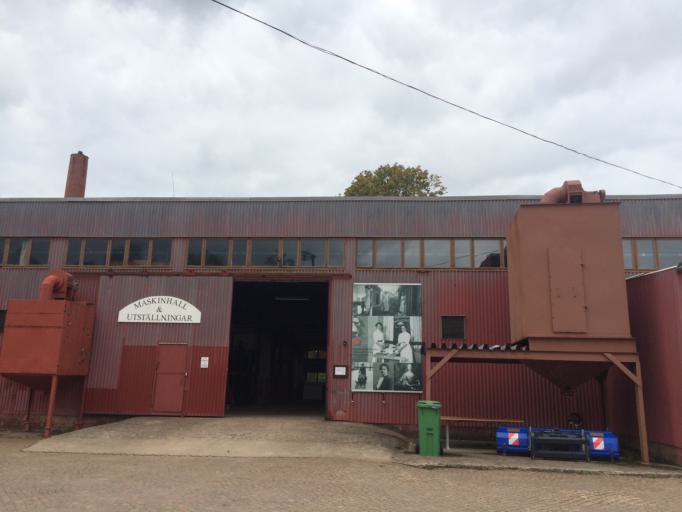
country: SE
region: Vaestra Goetaland
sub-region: Karlsborgs Kommun
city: Karlsborg
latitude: 58.5793
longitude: 14.4363
